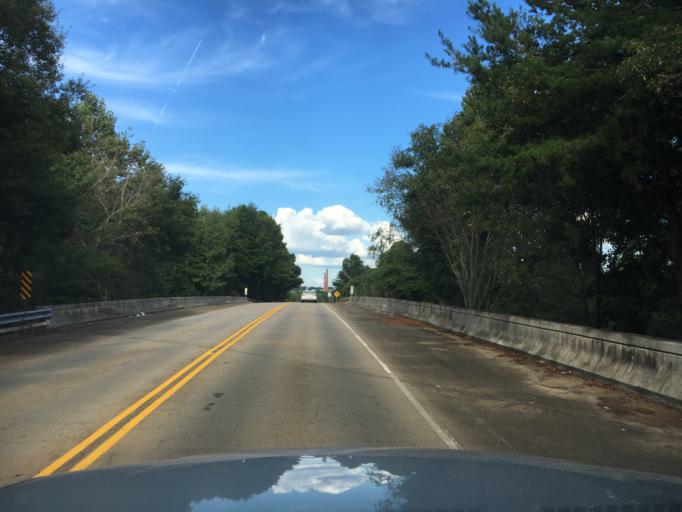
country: US
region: South Carolina
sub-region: Spartanburg County
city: Duncan
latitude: 34.9406
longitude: -82.1386
